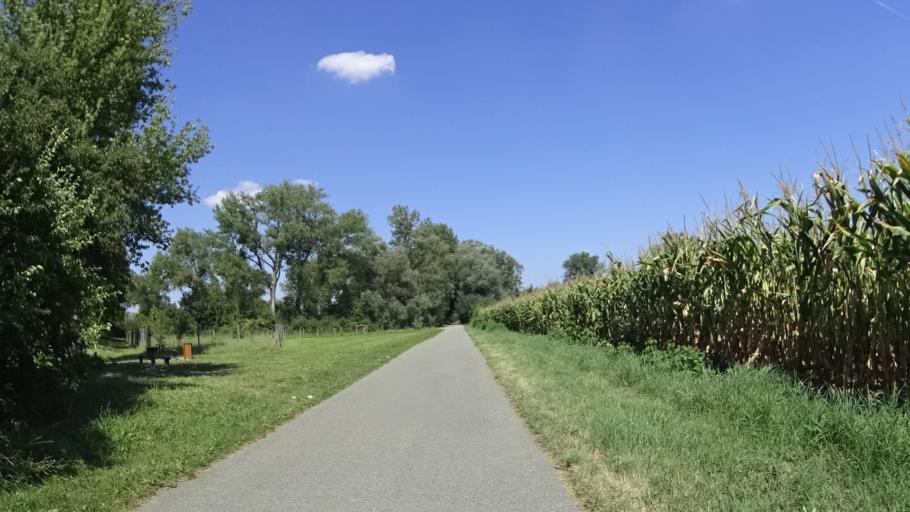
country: CZ
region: South Moravian
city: Straznice
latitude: 48.9139
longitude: 17.3272
